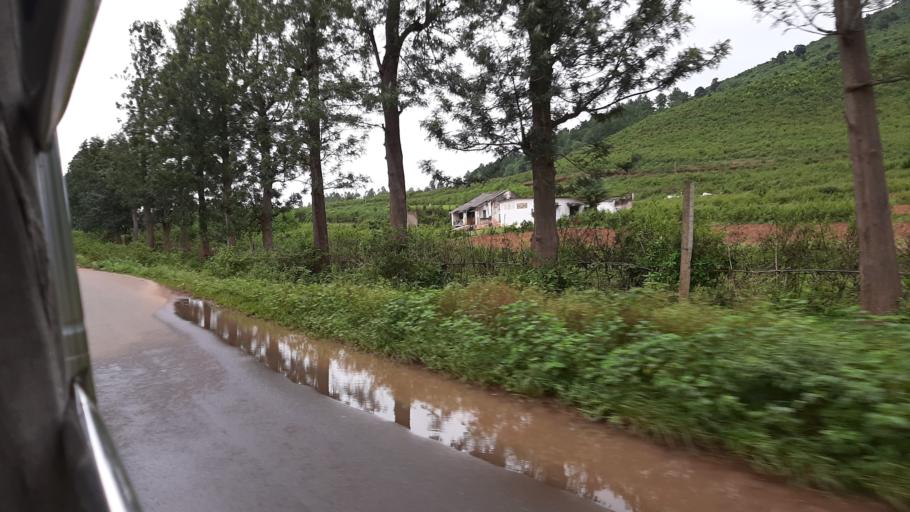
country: IN
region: Andhra Pradesh
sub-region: Vizianagaram District
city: Salur
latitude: 18.2943
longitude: 82.9170
